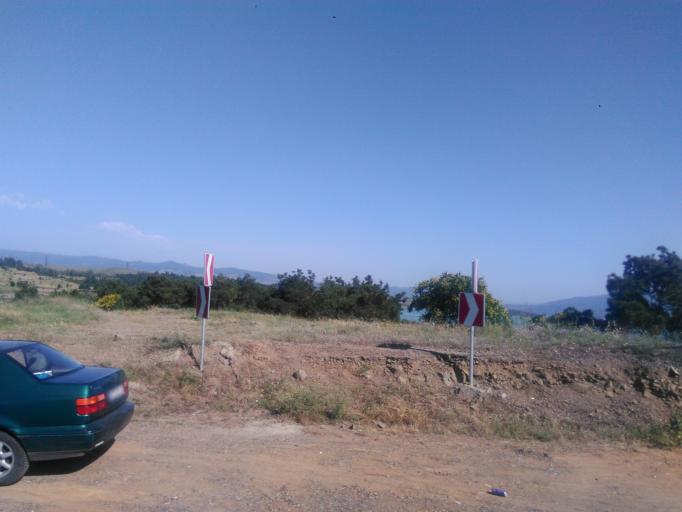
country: GE
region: T'bilisi
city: Tbilisi
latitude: 41.7394
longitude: 44.8402
